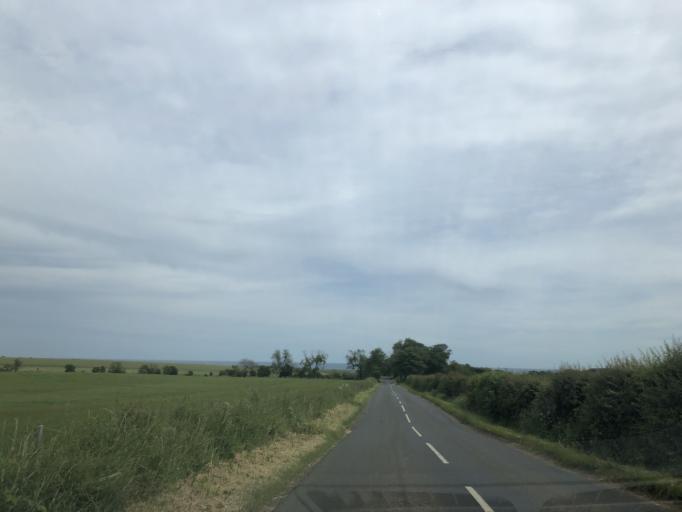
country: GB
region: Scotland
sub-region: Fife
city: Anstruther
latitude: 56.2656
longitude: -2.6425
